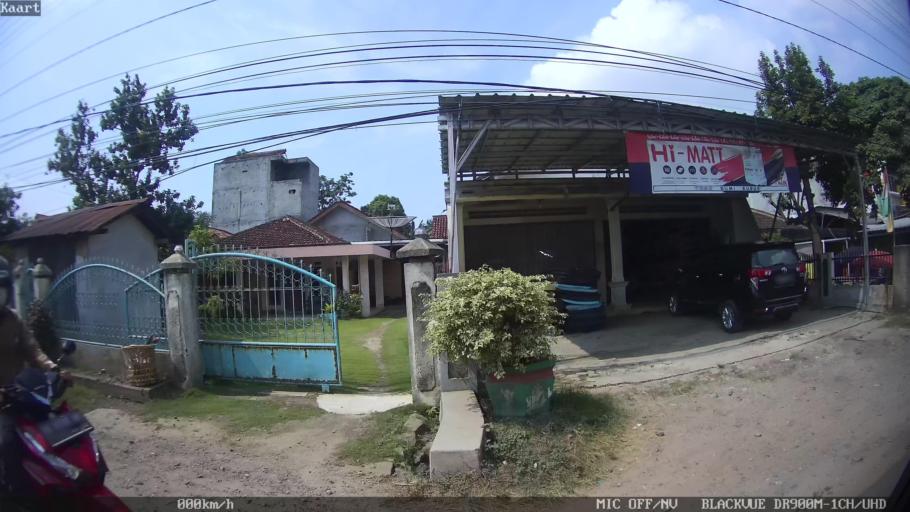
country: ID
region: Lampung
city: Pringsewu
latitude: -5.3575
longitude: 104.9866
